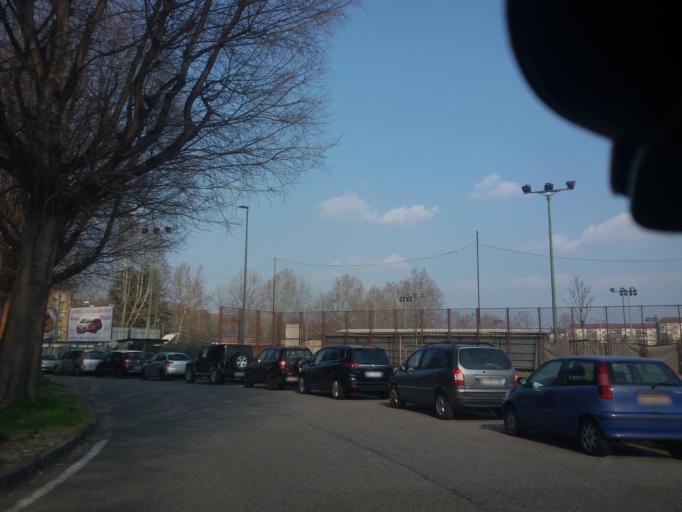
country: IT
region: Piedmont
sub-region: Provincia di Torino
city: Savonera
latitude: 45.1004
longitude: 7.6296
